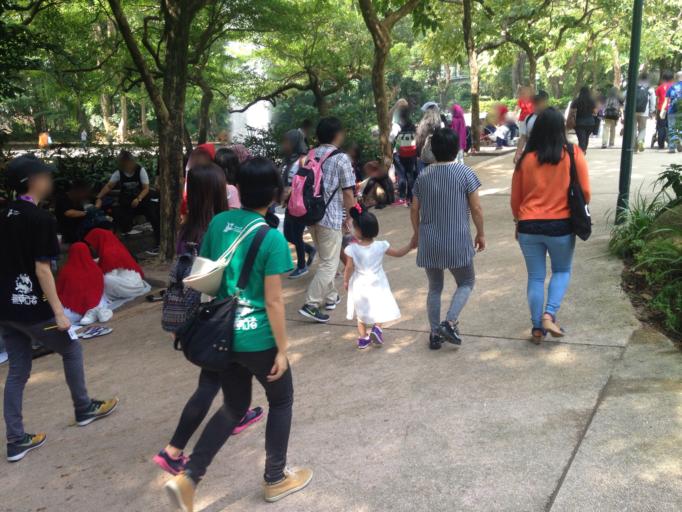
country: HK
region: Wanchai
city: Wan Chai
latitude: 22.2987
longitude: 114.1709
